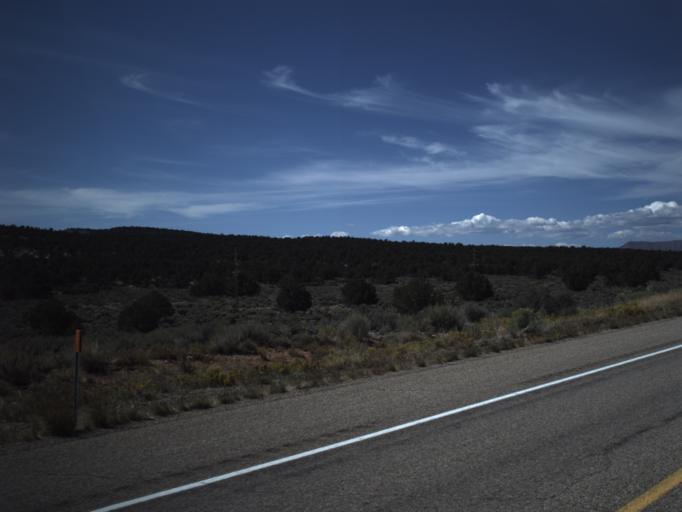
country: US
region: Utah
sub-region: Washington County
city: Ivins
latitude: 37.2749
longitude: -113.6467
